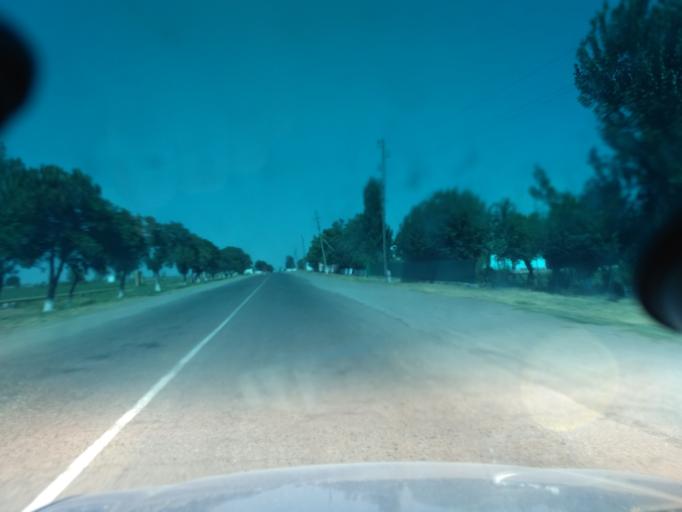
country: UZ
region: Sirdaryo
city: Guliston
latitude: 40.5008
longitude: 68.9471
